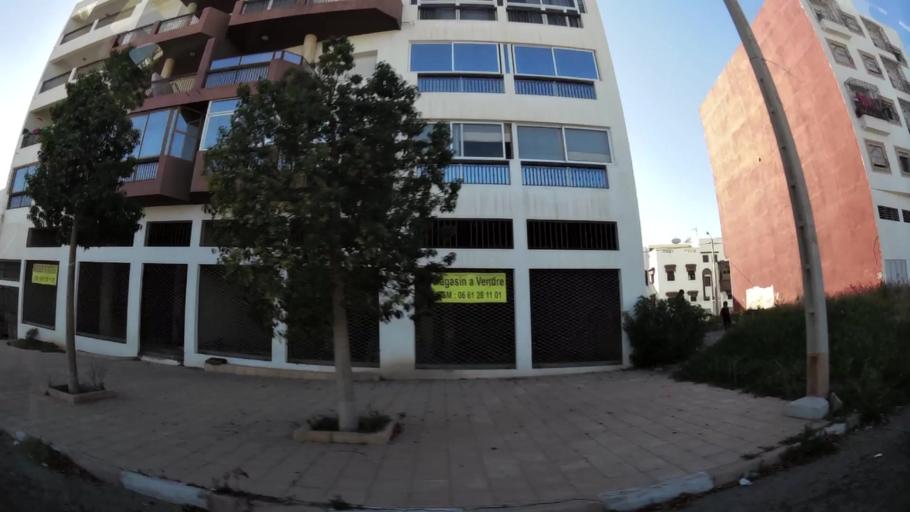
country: MA
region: Souss-Massa-Draa
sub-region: Agadir-Ida-ou-Tnan
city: Agadir
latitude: 30.4286
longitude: -9.5747
